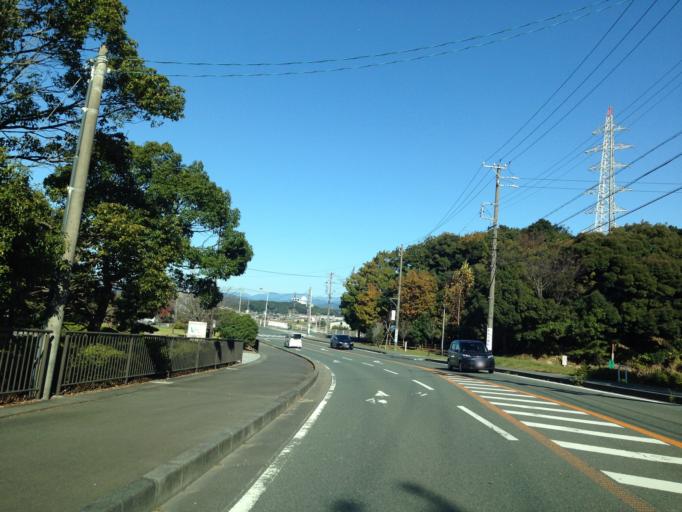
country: JP
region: Shizuoka
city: Fukuroi
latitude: 34.7438
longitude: 137.9430
